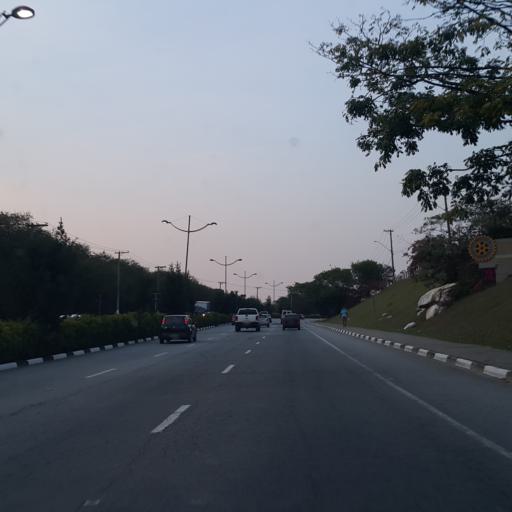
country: BR
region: Sao Paulo
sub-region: Vinhedo
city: Vinhedo
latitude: -23.0466
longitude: -46.9849
